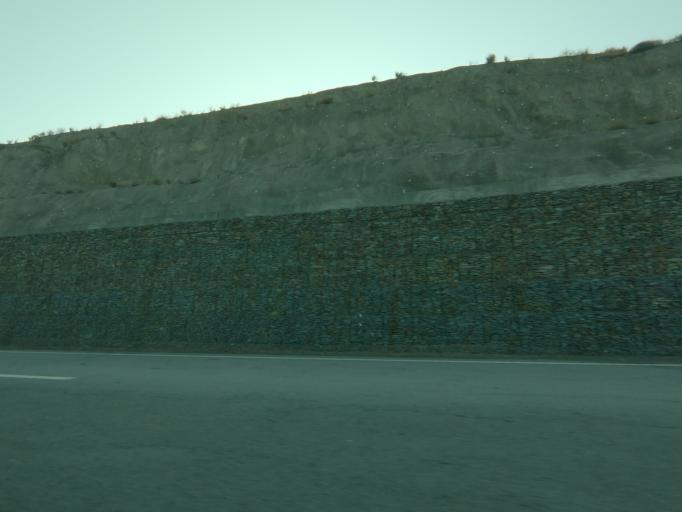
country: PT
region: Vila Real
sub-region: Peso da Regua
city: Peso da Regua
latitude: 41.1849
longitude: -7.7495
